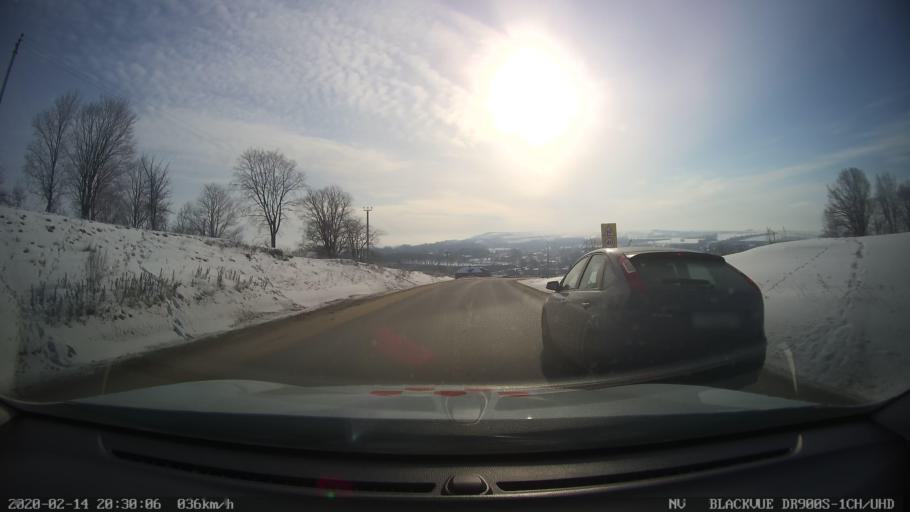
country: RU
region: Tatarstan
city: Stolbishchi
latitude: 55.4450
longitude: 48.9935
